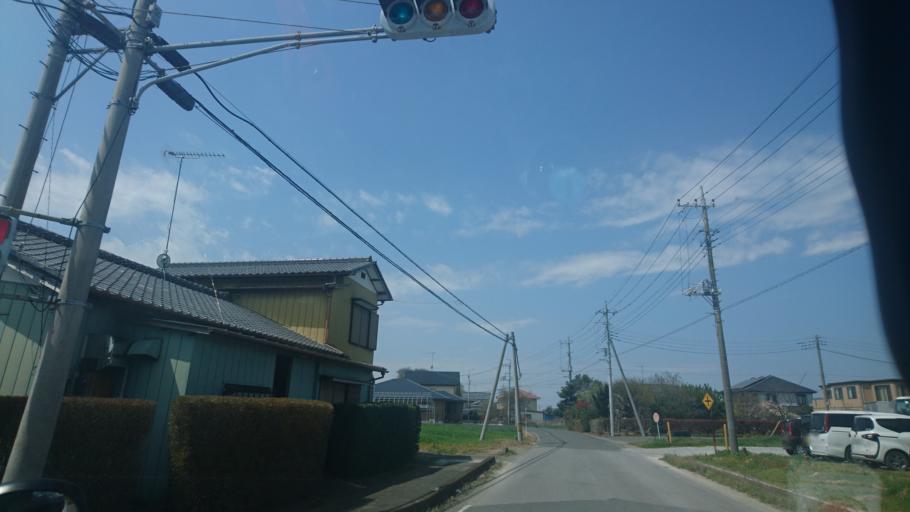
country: JP
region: Ibaraki
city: Yuki
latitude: 36.2205
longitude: 139.9235
